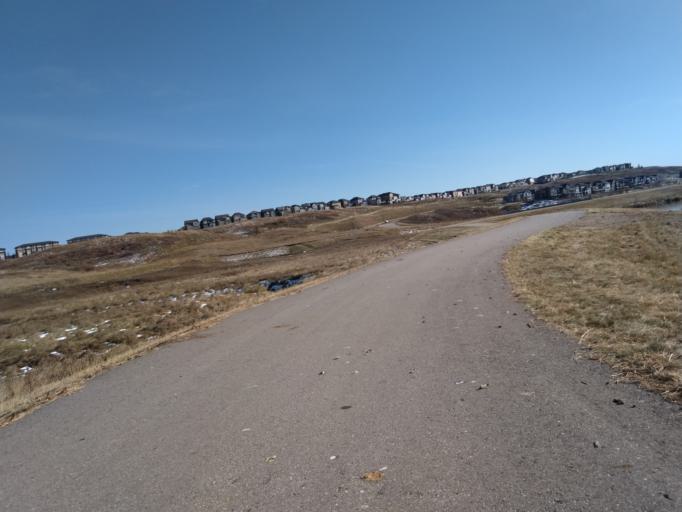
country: CA
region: Alberta
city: Calgary
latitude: 51.1796
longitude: -114.1305
